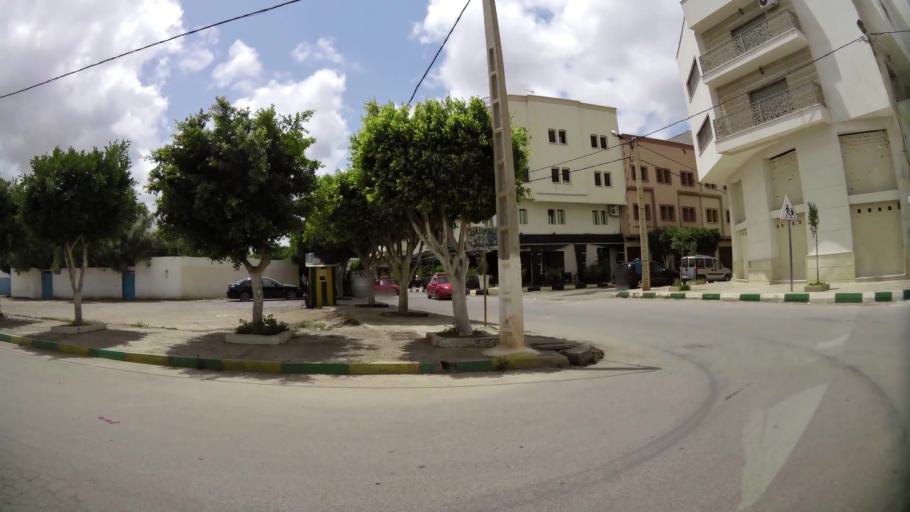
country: MA
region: Oriental
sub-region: Nador
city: Nador
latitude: 35.1674
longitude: -2.9170
